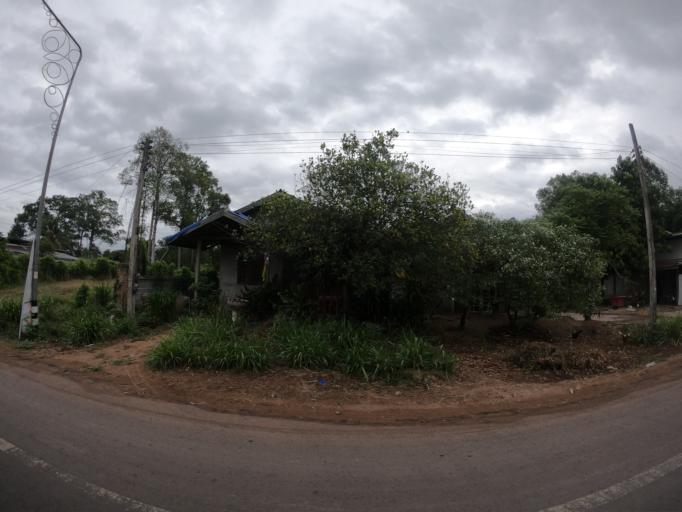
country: TH
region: Roi Et
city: Chiang Khwan
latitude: 16.1128
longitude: 103.8470
